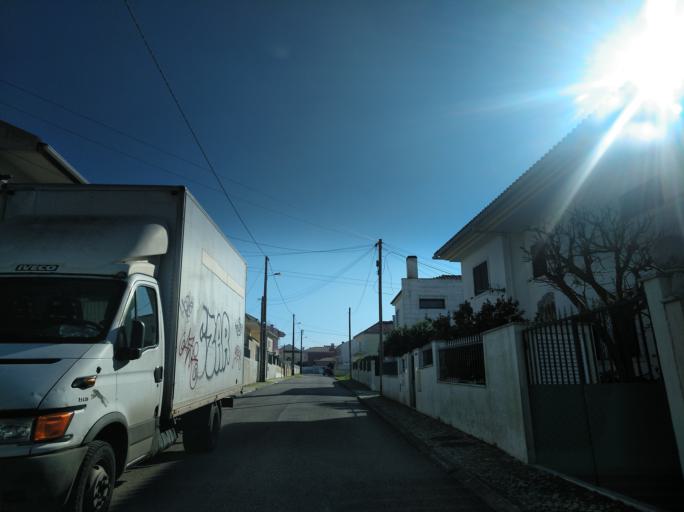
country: PT
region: Lisbon
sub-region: Odivelas
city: Canecas
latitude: 38.8061
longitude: -9.2183
